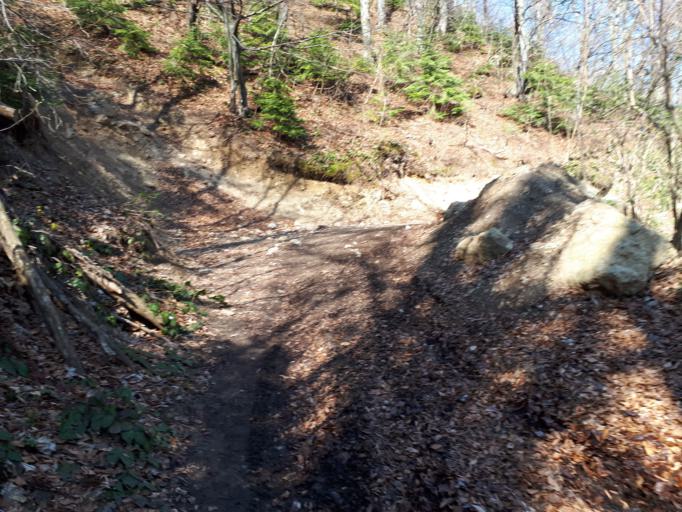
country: HR
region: Varazdinska
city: Ivanec
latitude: 46.1817
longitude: 16.1481
